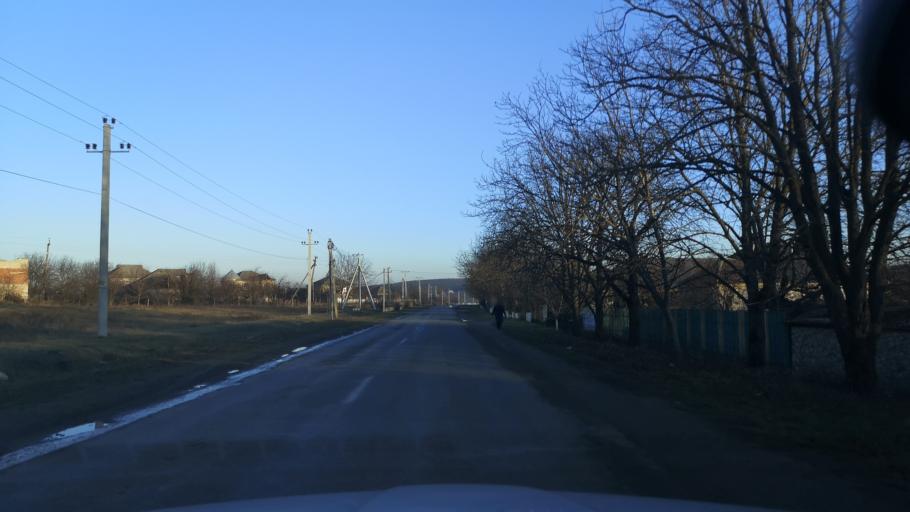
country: MD
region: Orhei
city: Orhei
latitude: 47.2876
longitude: 28.8642
